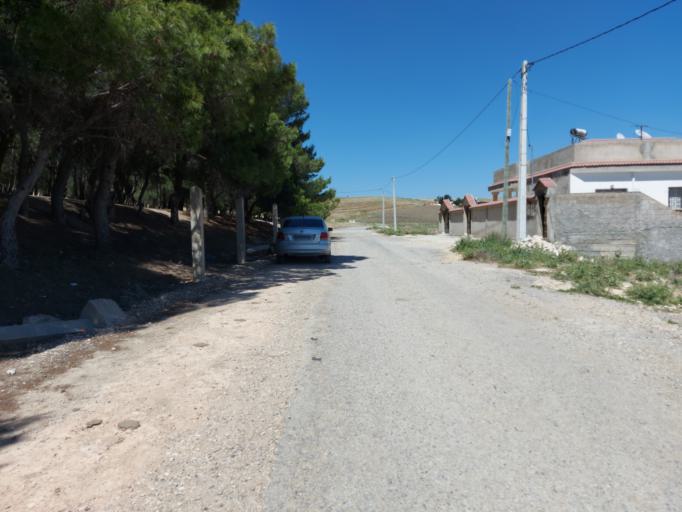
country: TN
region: Kef
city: El Kef
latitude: 36.1843
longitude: 8.7297
